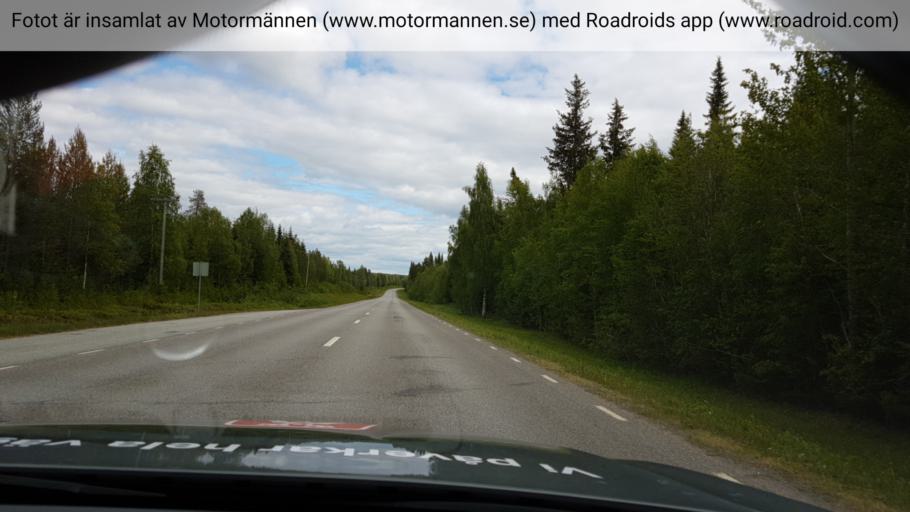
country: SE
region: Jaemtland
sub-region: Stroemsunds Kommun
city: Stroemsund
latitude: 64.2988
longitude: 15.3226
